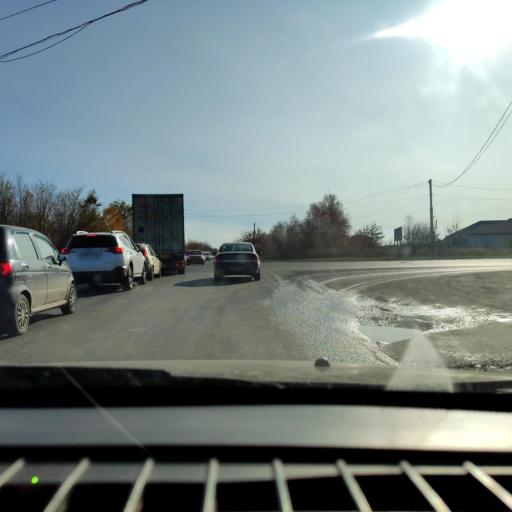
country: RU
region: Samara
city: Tol'yatti
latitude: 53.5607
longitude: 49.3578
